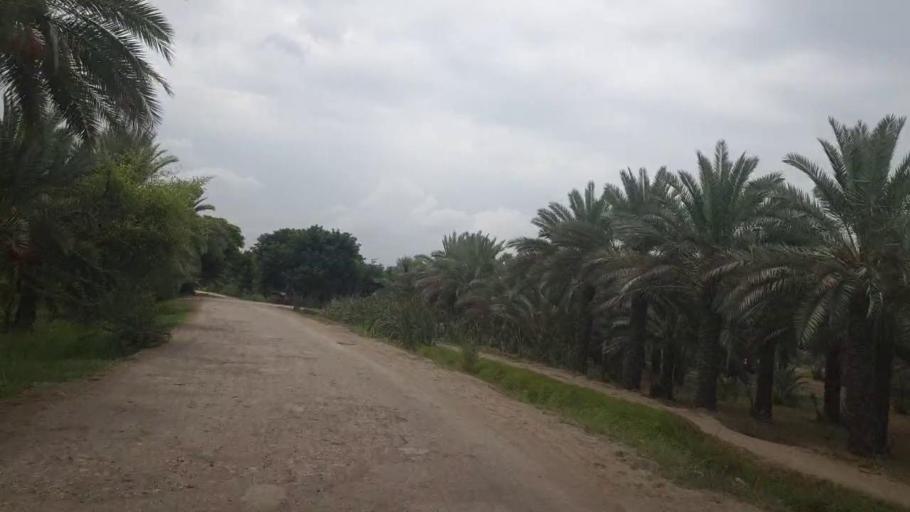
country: PK
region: Sindh
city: Khairpur
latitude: 27.5688
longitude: 68.7030
